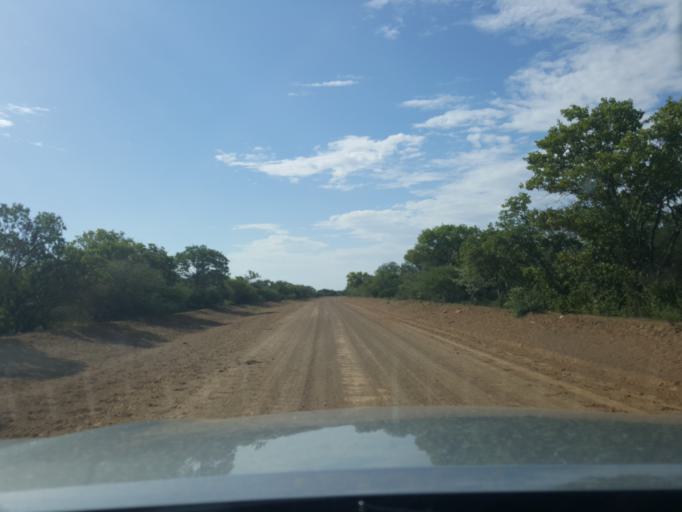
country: BW
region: Kweneng
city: Khudumelapye
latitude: -23.5321
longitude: 24.7248
